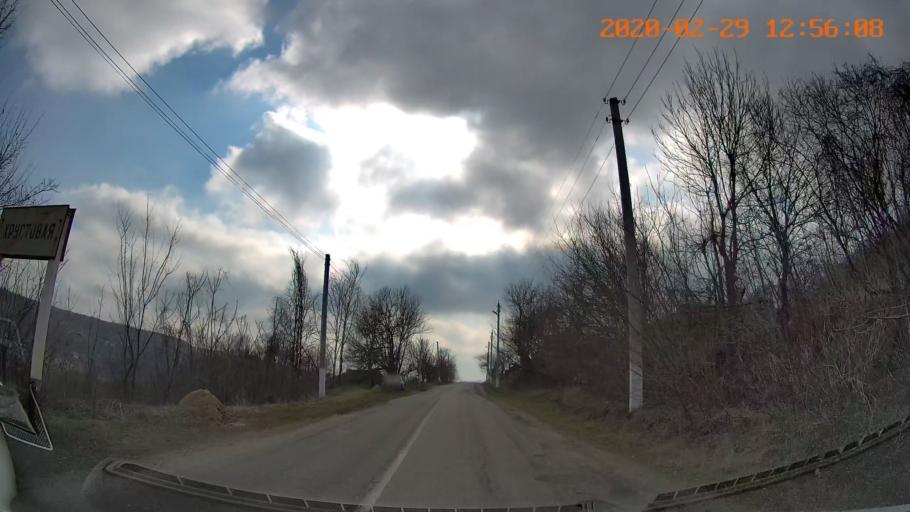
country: MD
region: Telenesti
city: Camenca
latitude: 48.0896
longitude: 28.7232
